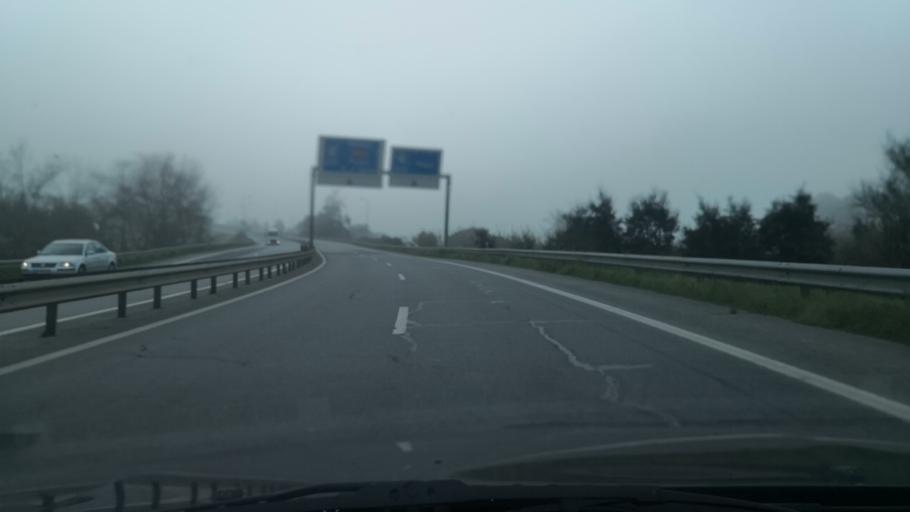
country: PT
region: Setubal
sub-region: Montijo
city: Montijo
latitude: 38.6822
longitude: -8.9482
